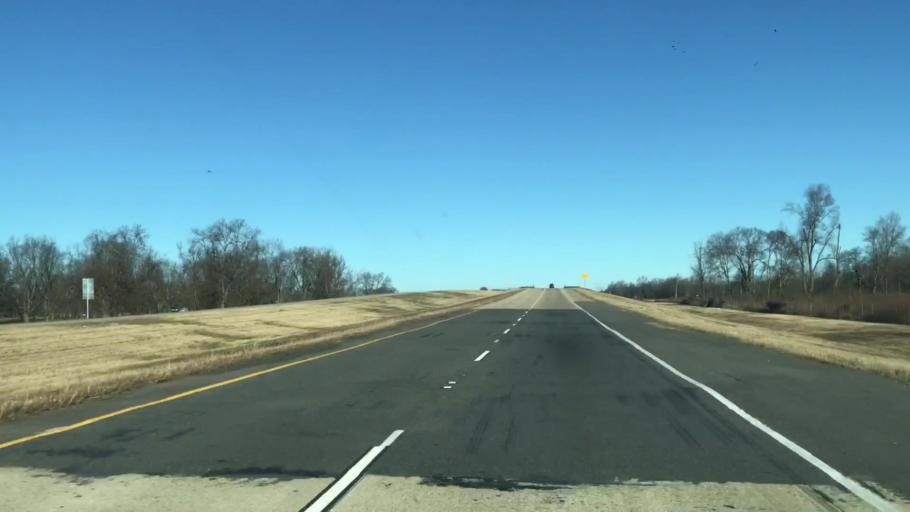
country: US
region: Louisiana
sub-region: Caddo Parish
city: Oil City
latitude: 32.7426
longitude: -93.8783
